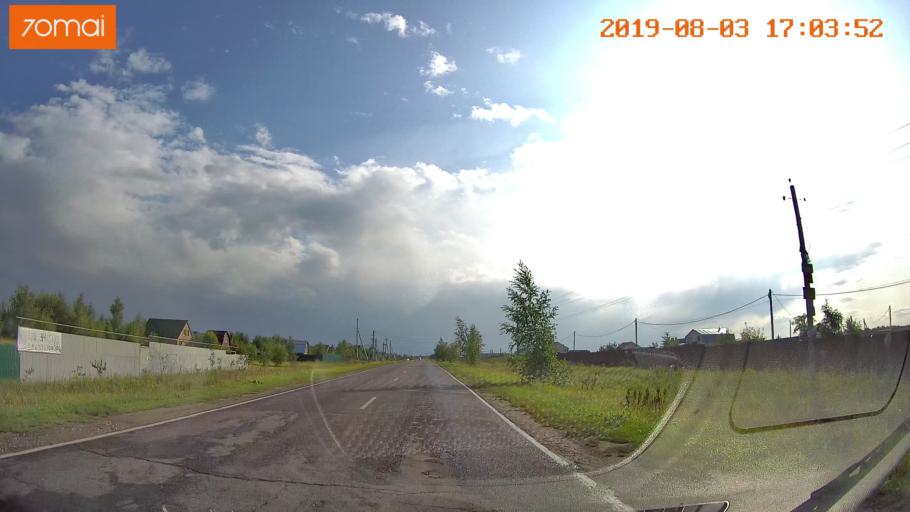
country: RU
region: Moskovskaya
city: Troitskoye
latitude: 55.3332
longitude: 38.5650
